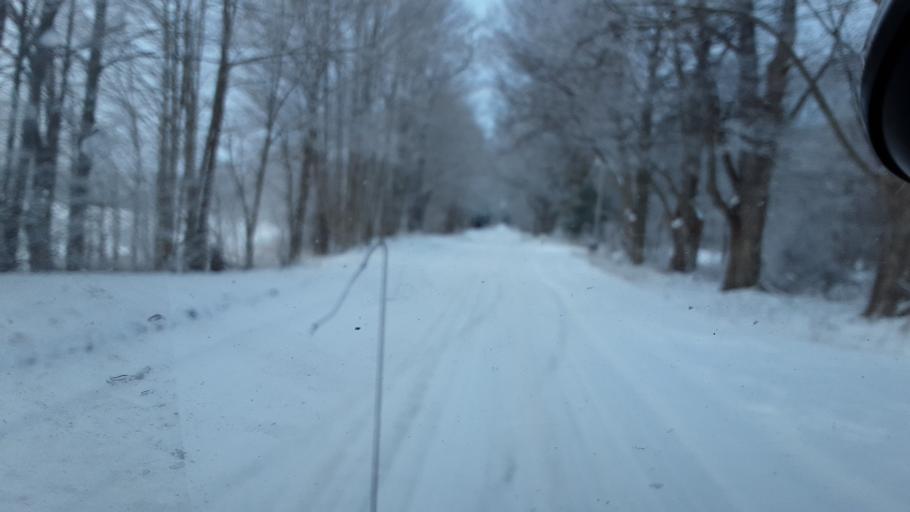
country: US
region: Michigan
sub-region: Ingham County
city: Leslie
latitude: 42.4222
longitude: -84.4834
